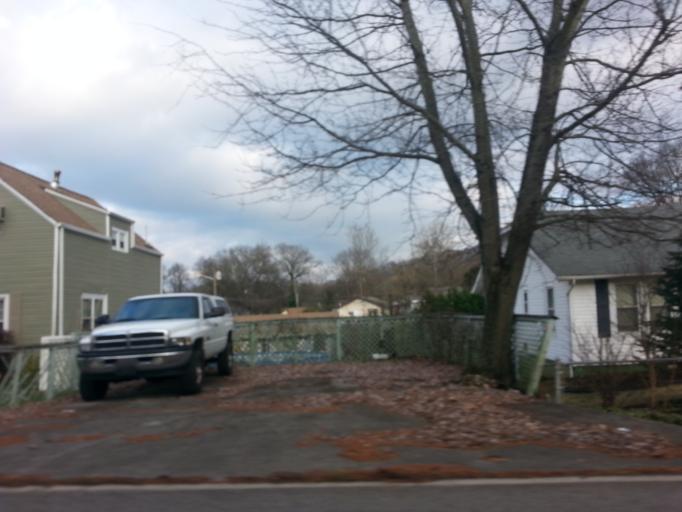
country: US
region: Tennessee
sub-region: Knox County
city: Knoxville
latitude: 35.9461
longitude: -83.8908
